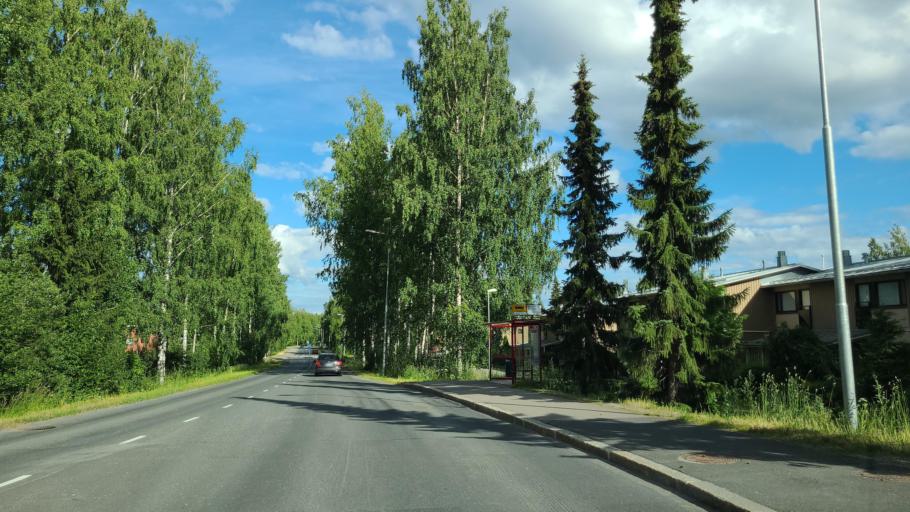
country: FI
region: Northern Savo
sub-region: Kuopio
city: Kuopio
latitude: 62.9380
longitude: 27.6497
